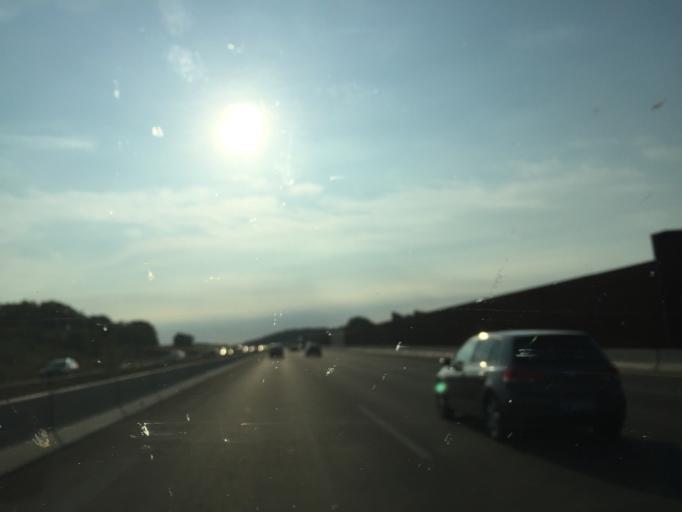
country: DE
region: Baden-Wuerttemberg
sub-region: Regierungsbezirk Stuttgart
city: Kirchardt
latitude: 49.2189
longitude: 8.9932
